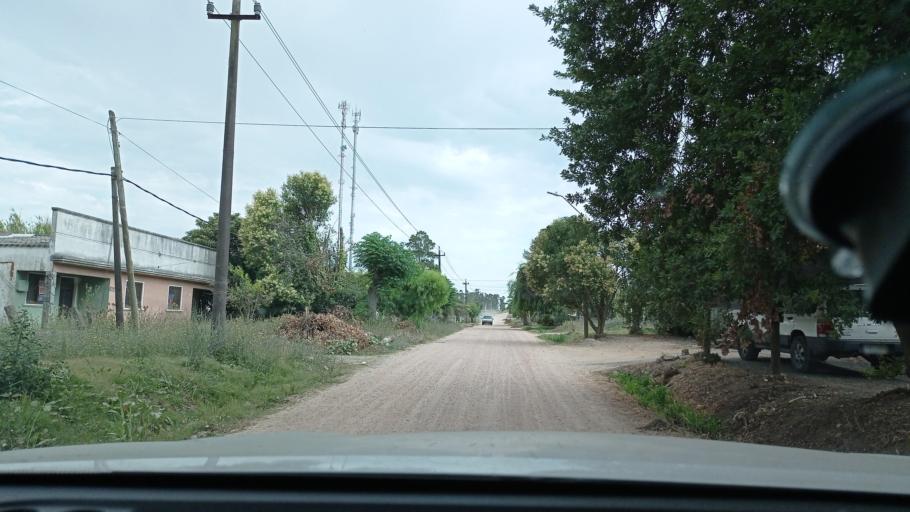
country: UY
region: Canelones
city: Pando
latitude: -34.7080
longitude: -55.9691
